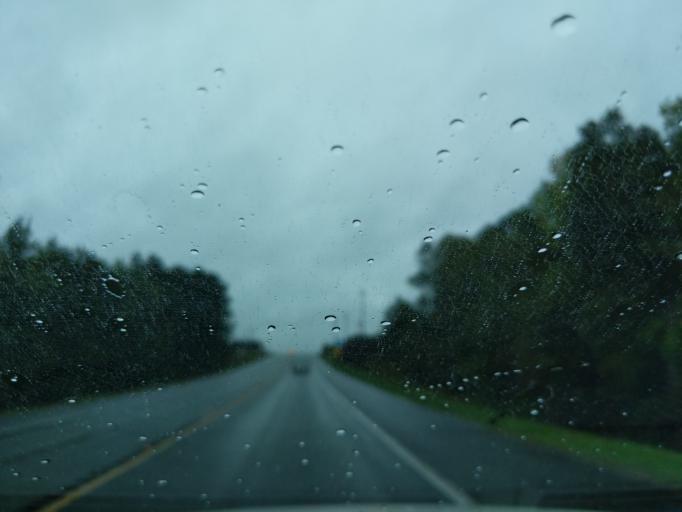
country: US
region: Louisiana
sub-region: Webster Parish
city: Minden
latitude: 32.6189
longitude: -93.2497
